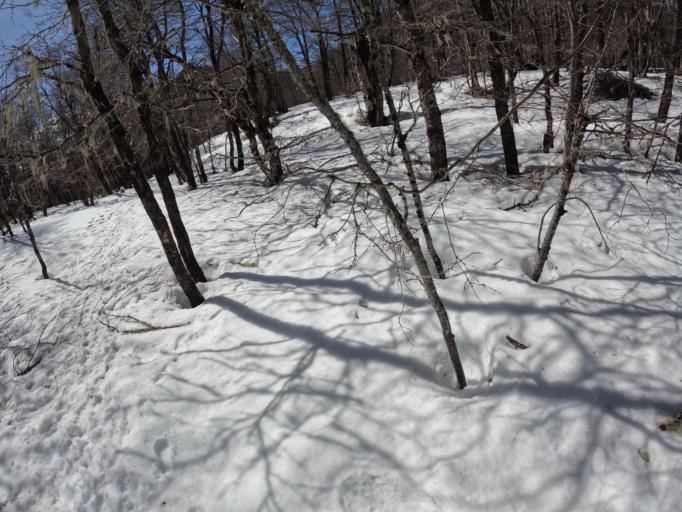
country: CL
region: Araucania
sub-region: Provincia de Cautin
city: Vilcun
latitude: -38.6499
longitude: -71.6187
